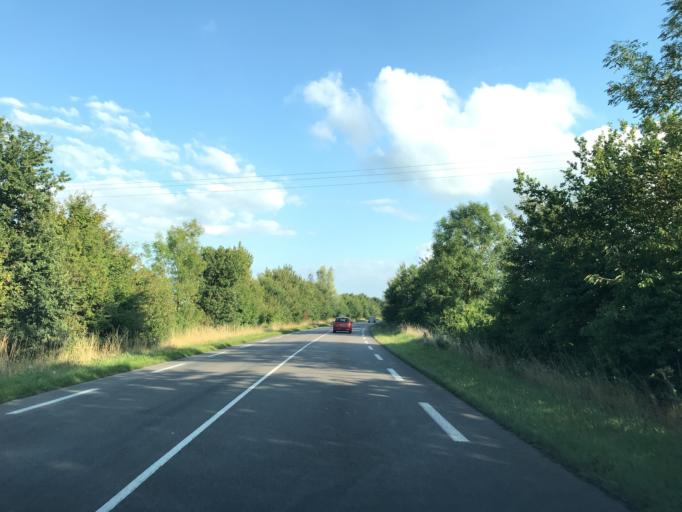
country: FR
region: Haute-Normandie
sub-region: Departement de la Seine-Maritime
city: Bolbec
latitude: 49.5791
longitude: 0.4522
